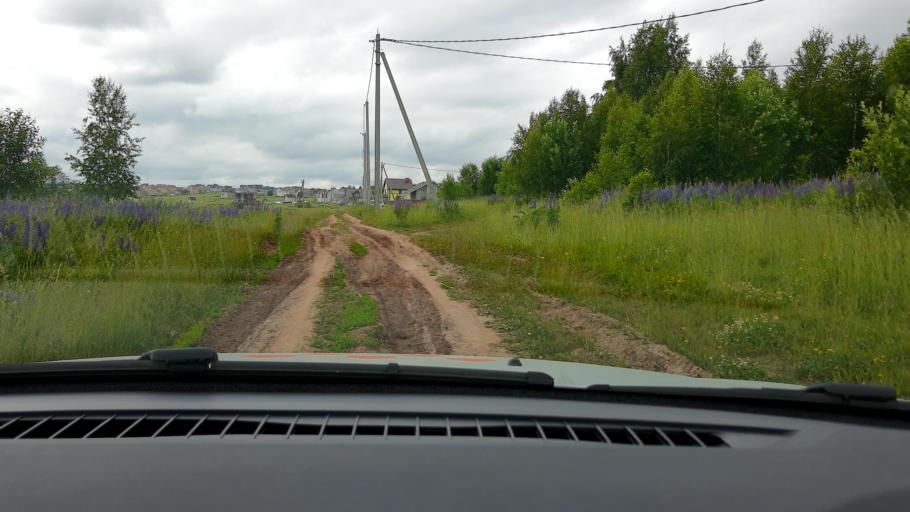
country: RU
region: Nizjnij Novgorod
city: Nizhniy Novgorod
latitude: 56.2268
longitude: 43.9905
